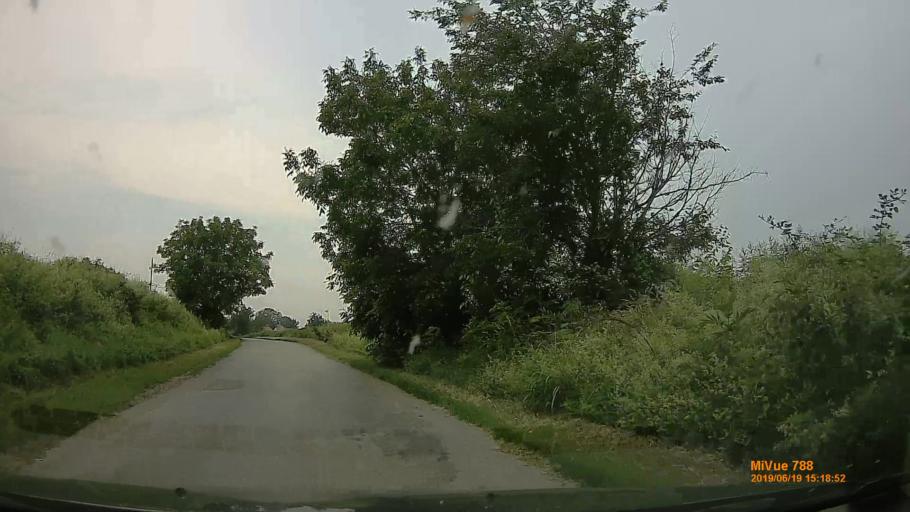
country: HU
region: Baranya
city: Szigetvar
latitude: 46.0753
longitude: 17.8573
